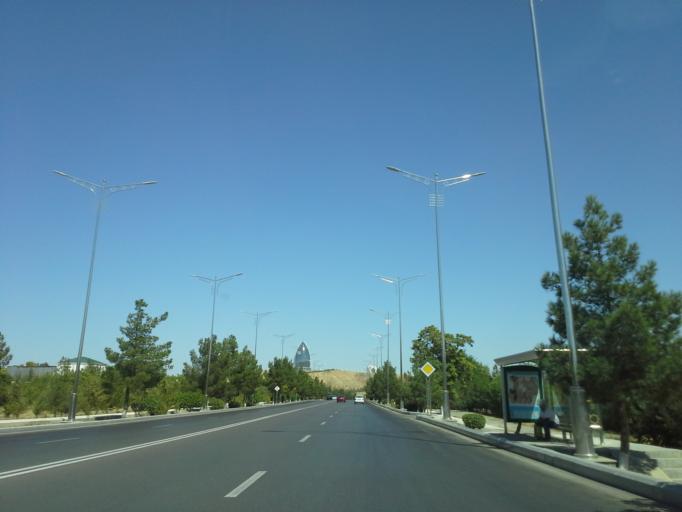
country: TM
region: Ahal
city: Ashgabat
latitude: 37.9298
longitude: 58.3066
